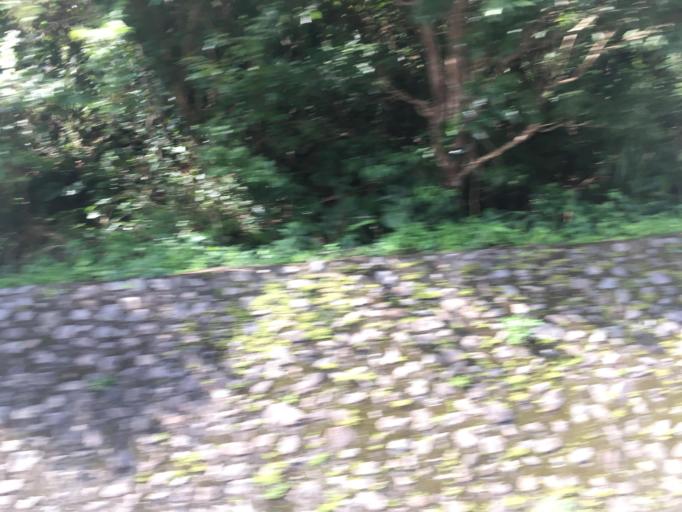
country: TW
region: Taiwan
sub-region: Yilan
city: Yilan
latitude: 24.6076
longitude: 121.5240
